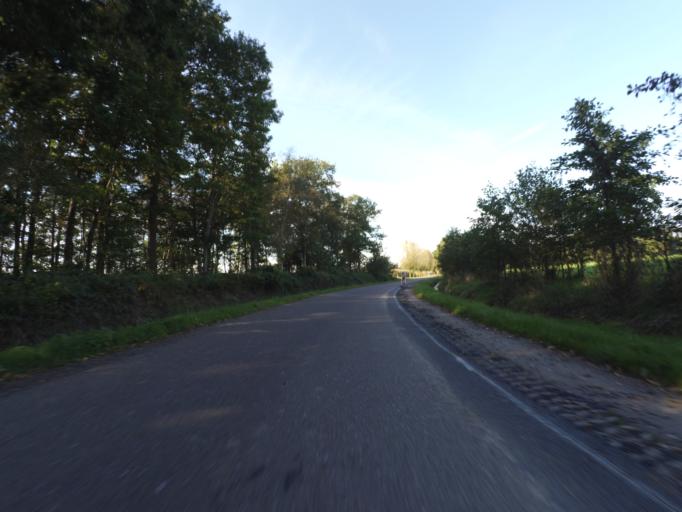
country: NL
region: Gelderland
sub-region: Gemeente Nijkerk
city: Nijkerk
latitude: 52.2249
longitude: 5.5101
